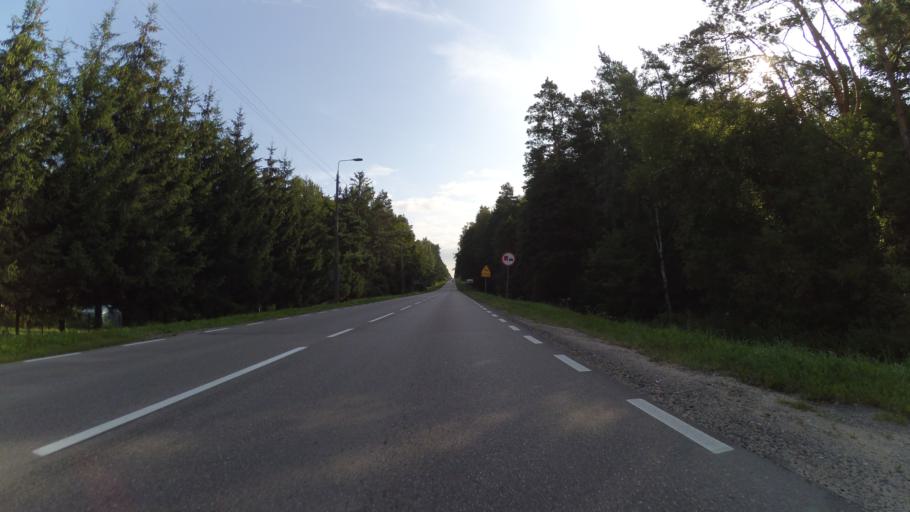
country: PL
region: Podlasie
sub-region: Powiat bialostocki
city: Czarna Bialostocka
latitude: 53.3025
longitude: 23.3058
